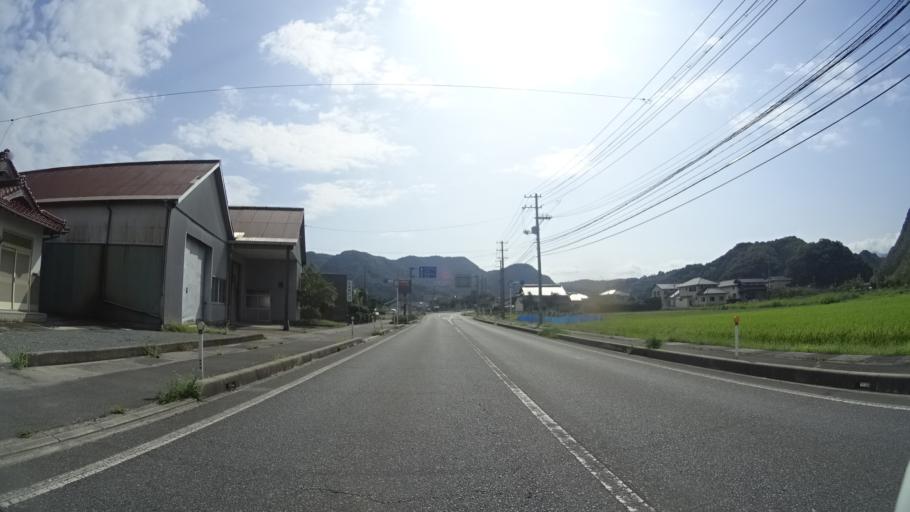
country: JP
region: Shimane
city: Odacho-oda
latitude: 35.1476
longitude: 132.4074
